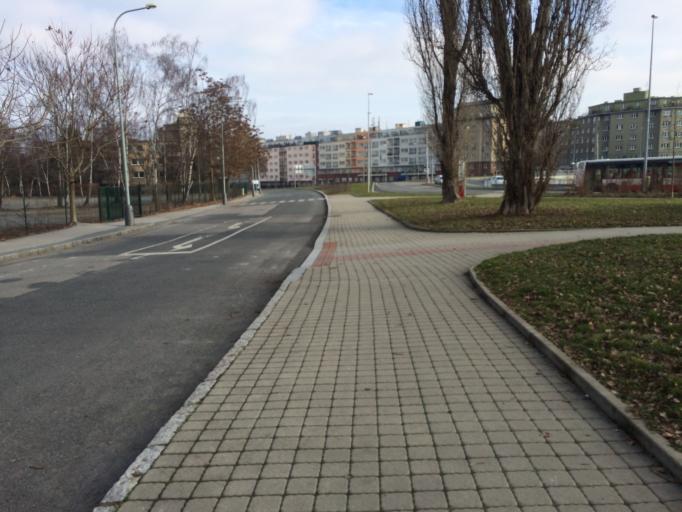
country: CZ
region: Praha
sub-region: Praha 1
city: Mala Strana
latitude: 50.0891
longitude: 14.3804
